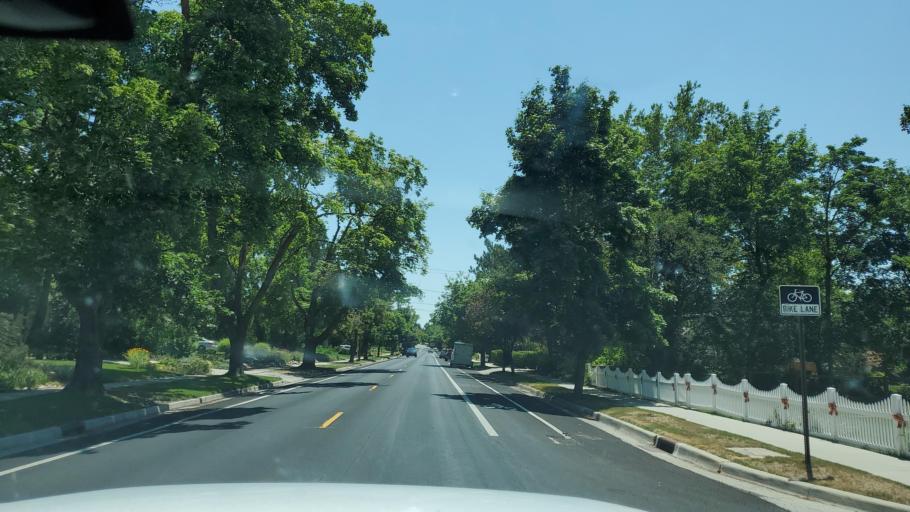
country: US
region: Utah
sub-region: Salt Lake County
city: Willard
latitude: 40.7231
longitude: -111.8309
